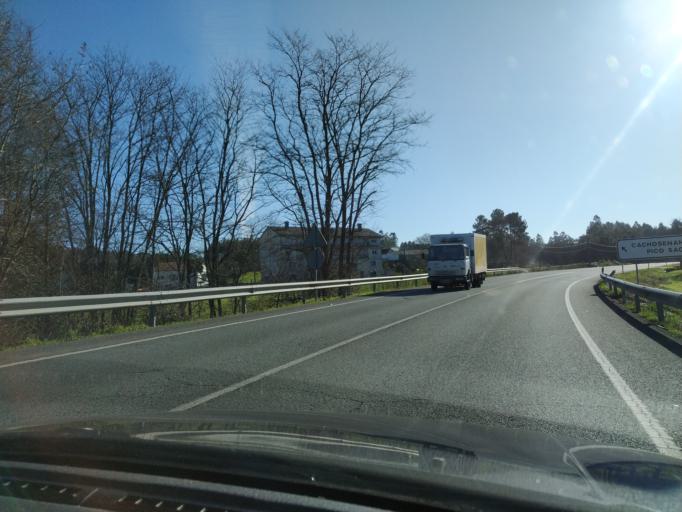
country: ES
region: Galicia
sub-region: Provincia da Coruna
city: Vedra
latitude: 42.7950
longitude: -8.4636
